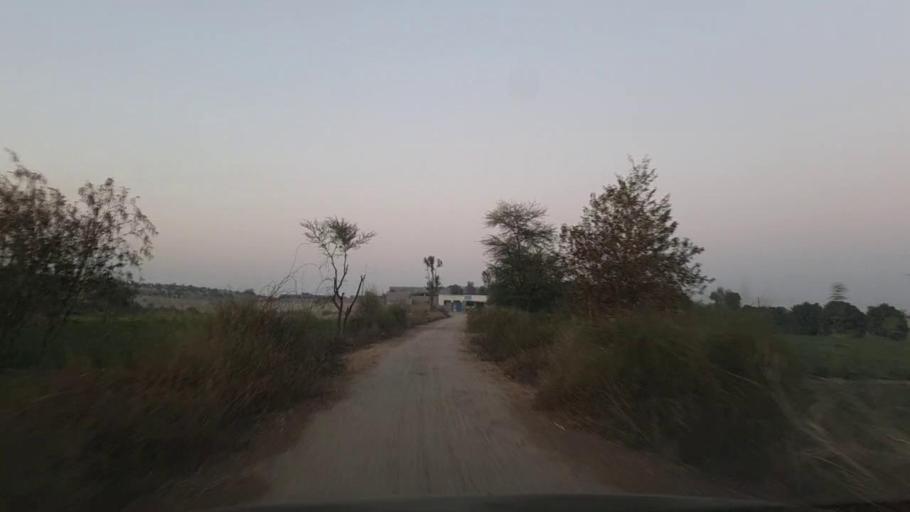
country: PK
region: Sindh
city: Daur
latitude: 26.4835
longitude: 68.4835
